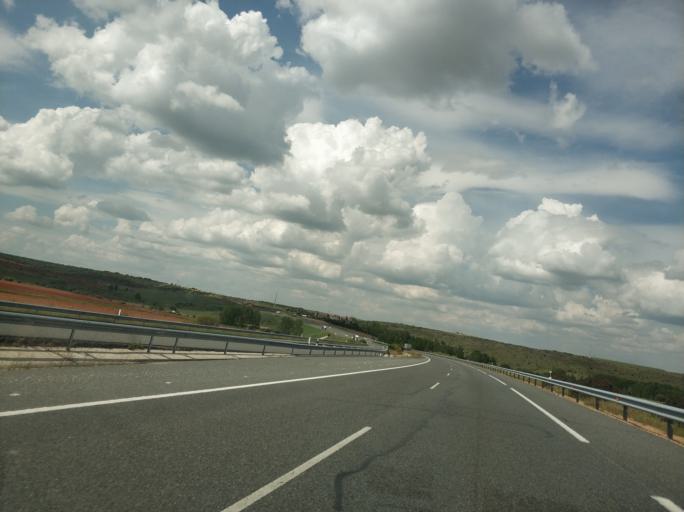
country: ES
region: Castille and Leon
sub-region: Provincia de Salamanca
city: Belena
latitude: 40.7385
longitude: -5.6303
